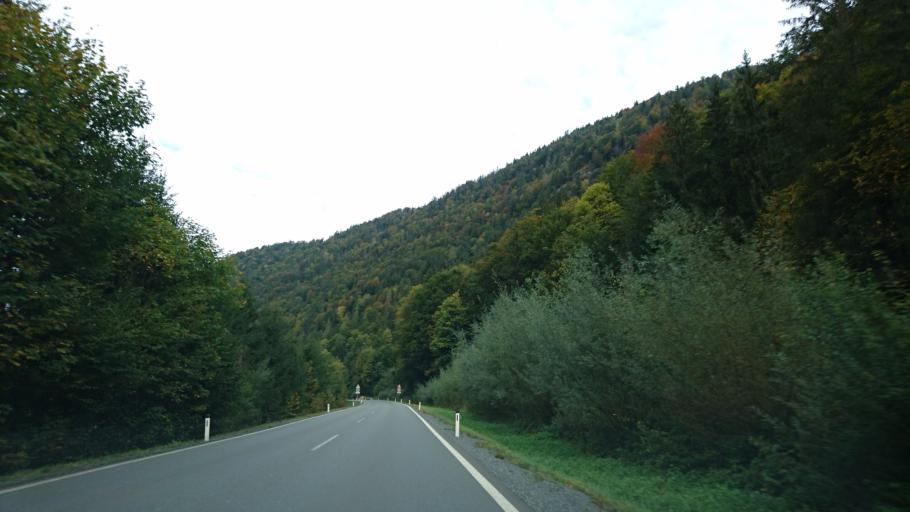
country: DE
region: Bavaria
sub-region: Upper Bavaria
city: Reit im Winkl
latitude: 47.6416
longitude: 12.4533
